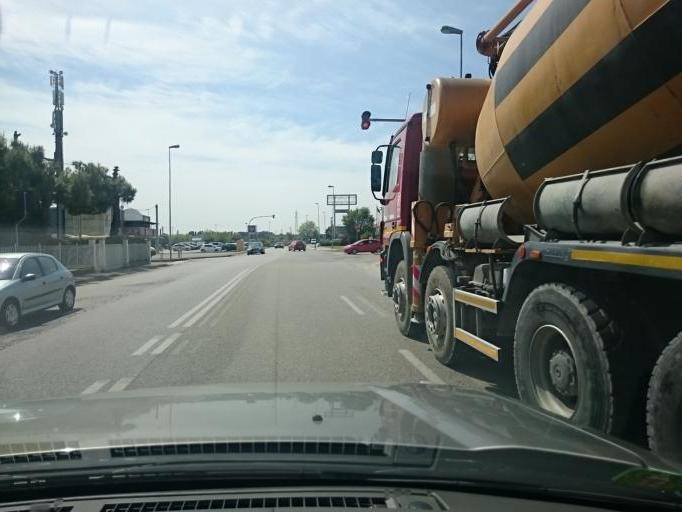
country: IT
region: Veneto
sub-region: Provincia di Padova
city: Monselice
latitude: 45.2286
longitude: 11.7453
